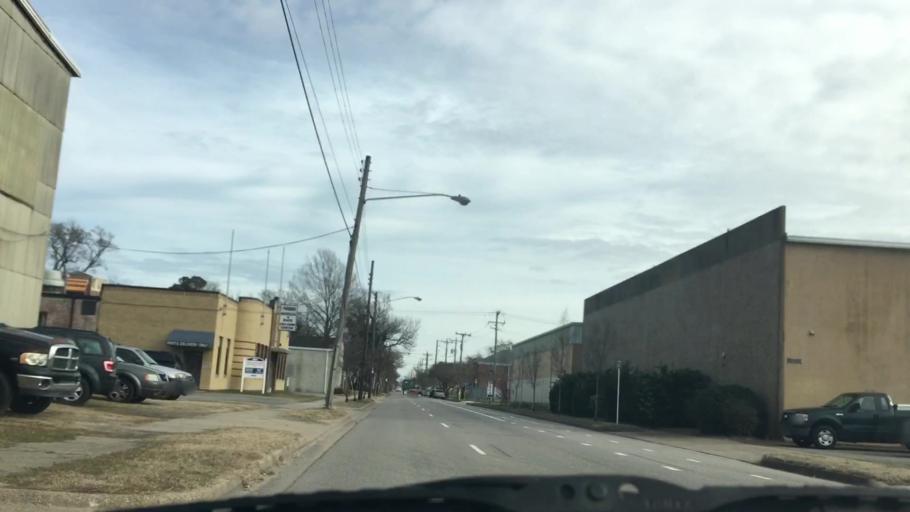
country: US
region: Virginia
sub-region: City of Norfolk
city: Norfolk
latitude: 36.8757
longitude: -76.2996
